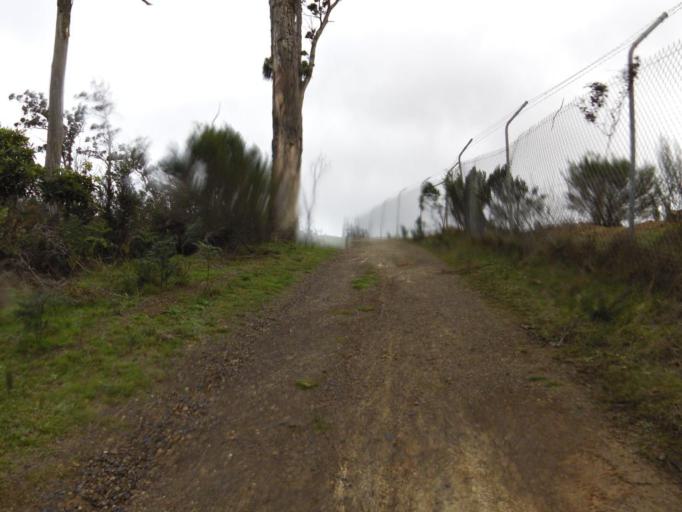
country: AU
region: Victoria
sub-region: Yarra Ranges
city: Lysterfield
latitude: -37.9337
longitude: 145.2774
